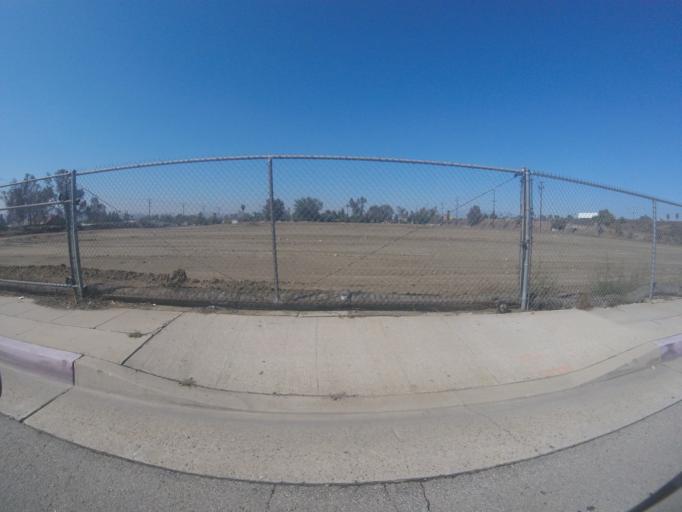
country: US
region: California
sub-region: San Bernardino County
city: Redlands
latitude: 34.0603
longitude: -117.1865
